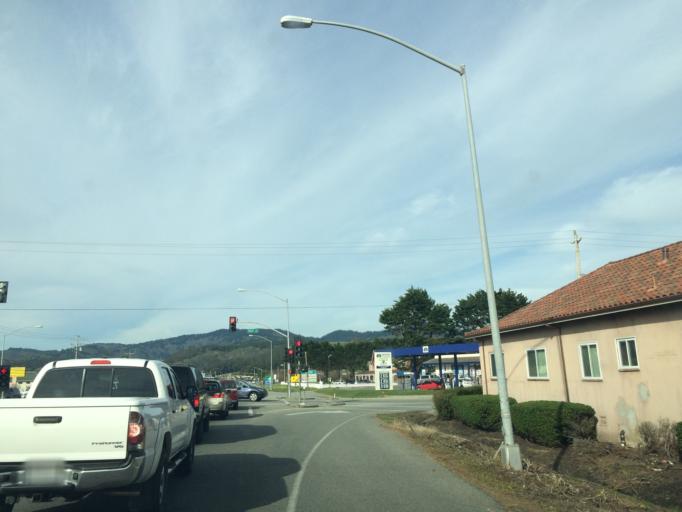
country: US
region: California
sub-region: San Mateo County
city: Half Moon Bay
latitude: 37.4637
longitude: -122.4341
